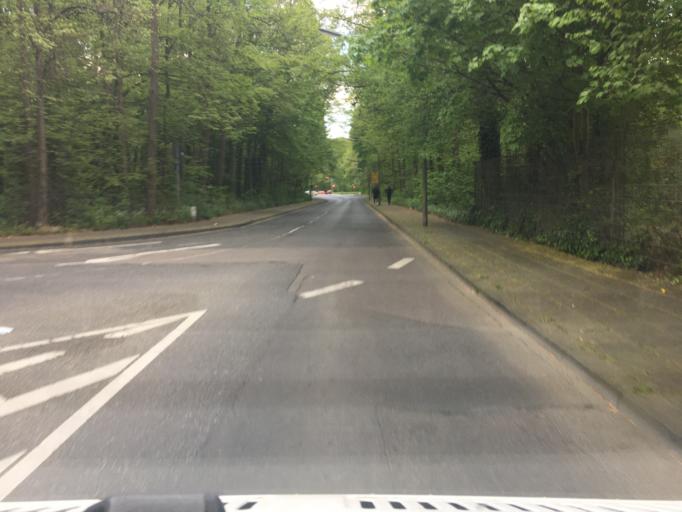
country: DE
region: North Rhine-Westphalia
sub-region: Regierungsbezirk Koln
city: Mengenich
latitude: 50.9840
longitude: 6.8709
